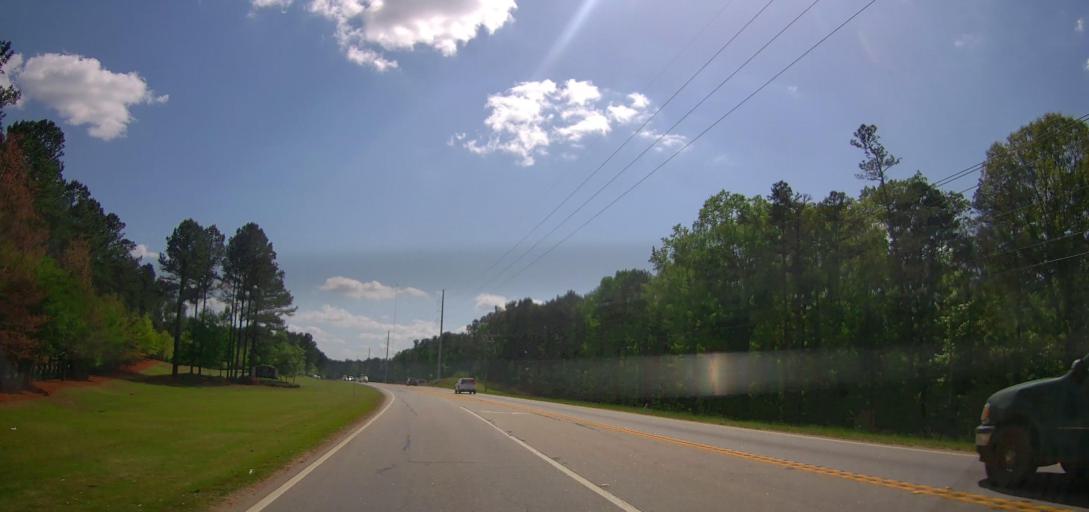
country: US
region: Georgia
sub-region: Putnam County
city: Jefferson
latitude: 33.4795
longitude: -83.2420
